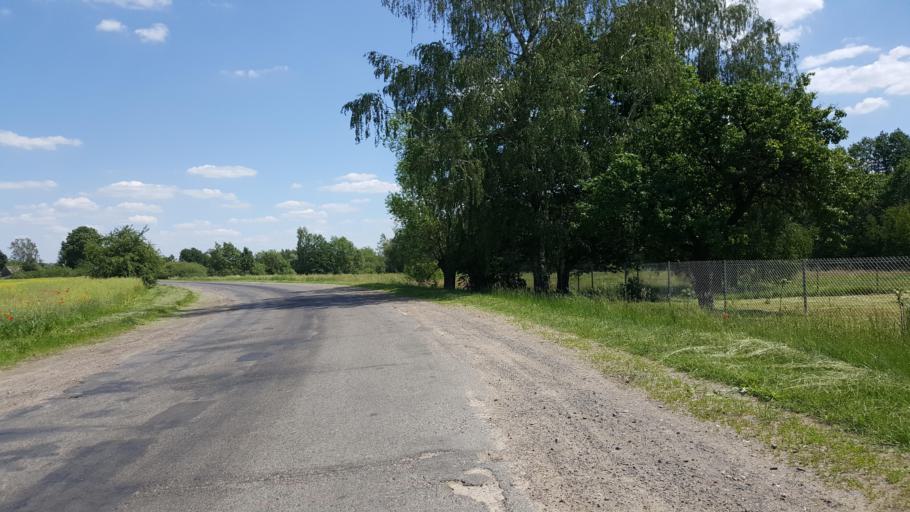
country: BY
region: Brest
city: Zhabinka
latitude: 52.1956
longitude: 24.1719
